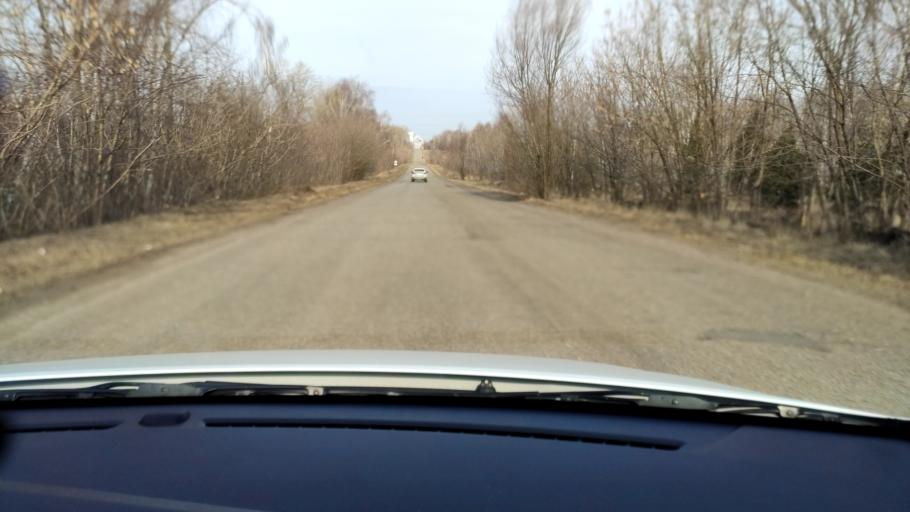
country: RU
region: Tatarstan
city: Stolbishchi
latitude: 55.7194
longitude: 49.2136
